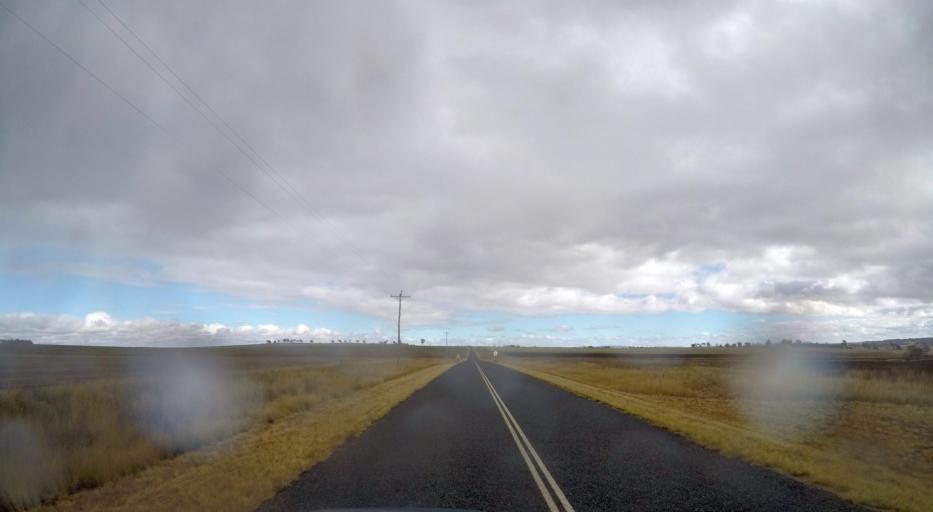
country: AU
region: Queensland
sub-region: Southern Downs
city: Warwick
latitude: -28.0543
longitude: 152.0258
